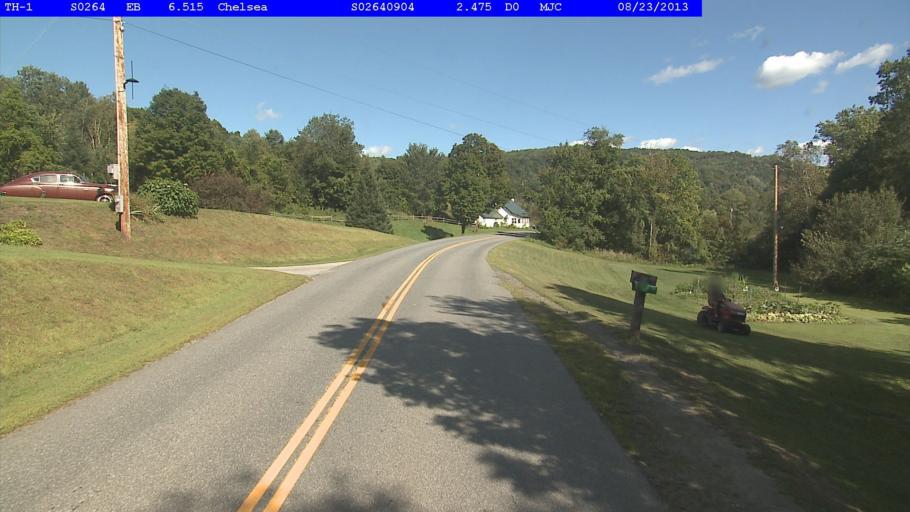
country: US
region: Vermont
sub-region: Orange County
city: Chelsea
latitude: 43.9633
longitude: -72.4718
